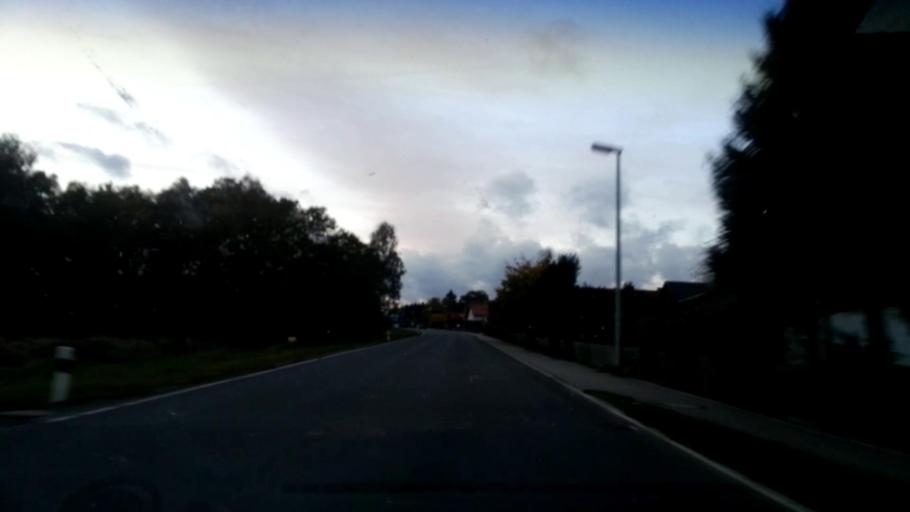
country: DE
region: Bavaria
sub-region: Upper Franconia
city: Fichtelberg
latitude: 50.0001
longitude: 11.8455
